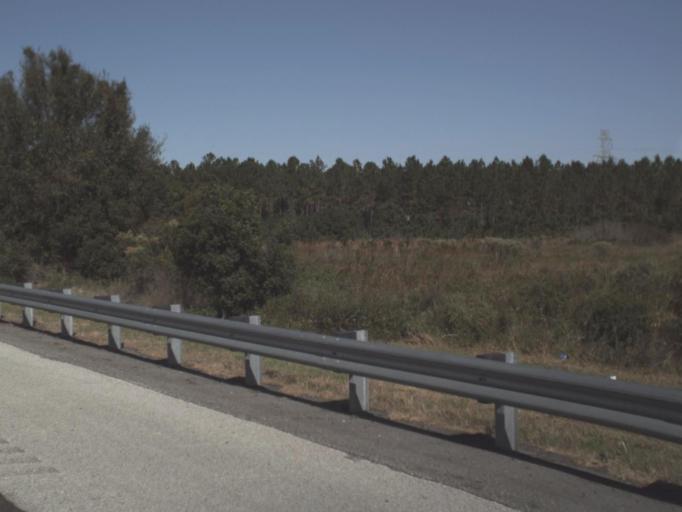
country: US
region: Florida
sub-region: Lake County
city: Hawthorne
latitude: 28.7397
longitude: -81.9220
